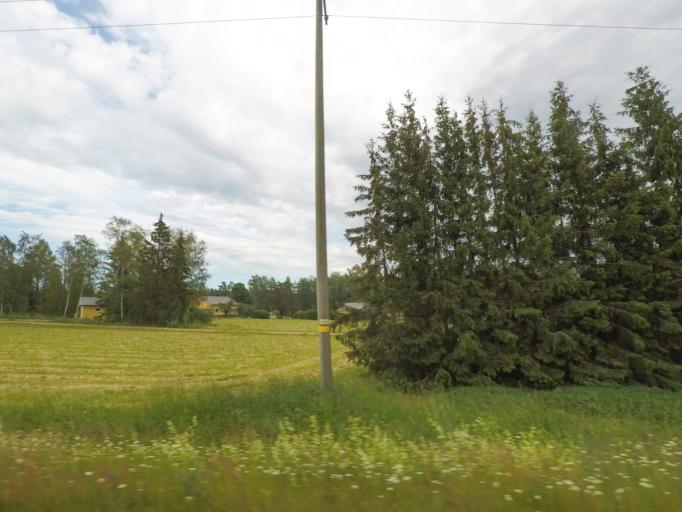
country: FI
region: Uusimaa
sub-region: Porvoo
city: Pukkila
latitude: 60.7616
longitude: 25.4420
